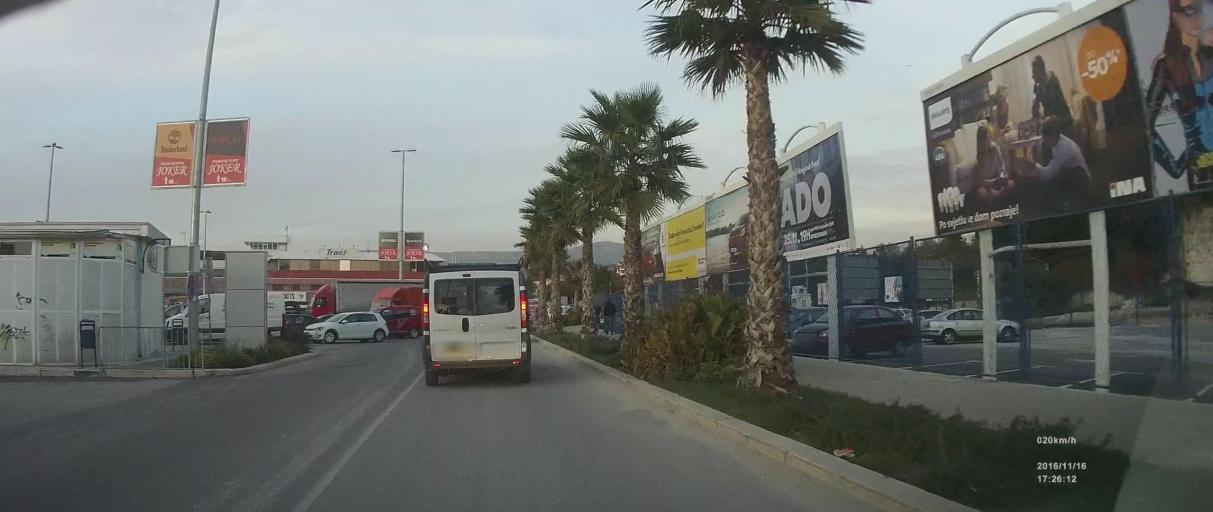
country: HR
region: Splitsko-Dalmatinska
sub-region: Grad Split
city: Split
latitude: 43.5018
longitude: 16.4423
